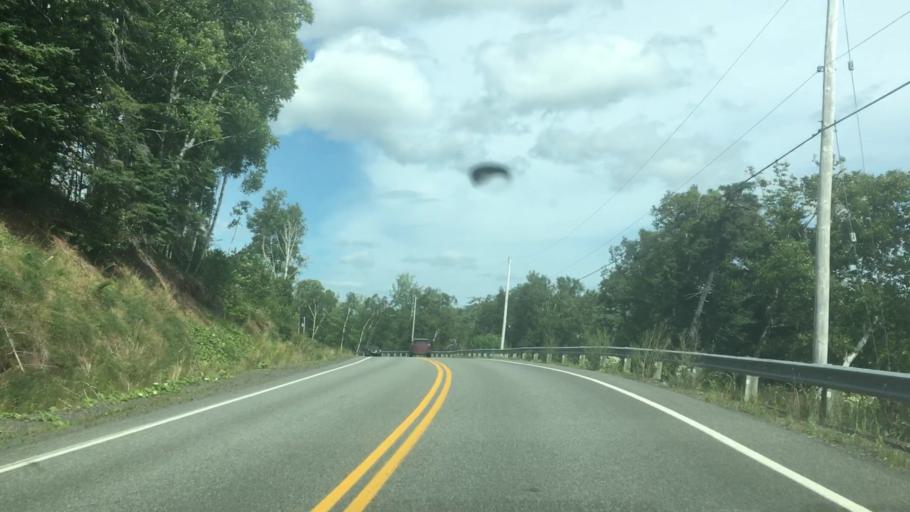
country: CA
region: Nova Scotia
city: Sydney Mines
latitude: 46.2669
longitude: -60.6087
